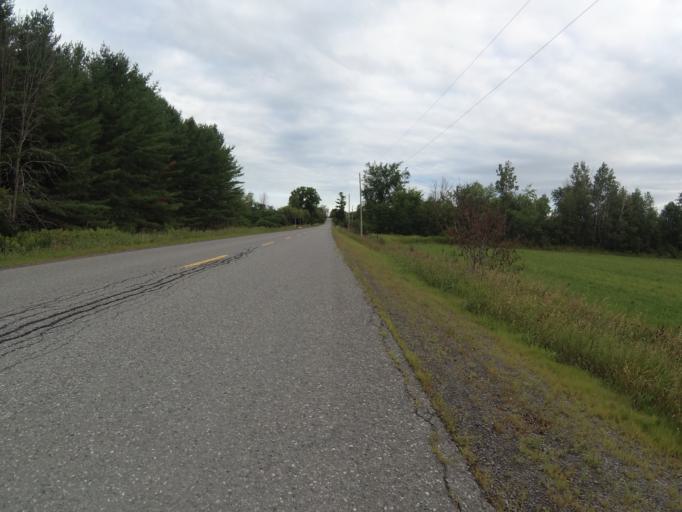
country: CA
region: Ontario
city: Clarence-Rockland
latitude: 45.4214
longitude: -75.2951
